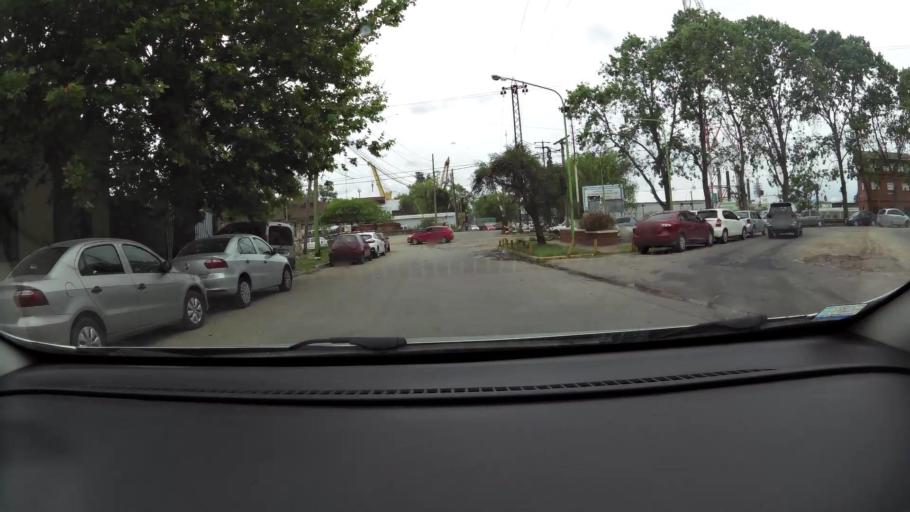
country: AR
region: Buenos Aires
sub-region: Partido de Campana
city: Campana
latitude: -34.1576
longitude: -58.9553
